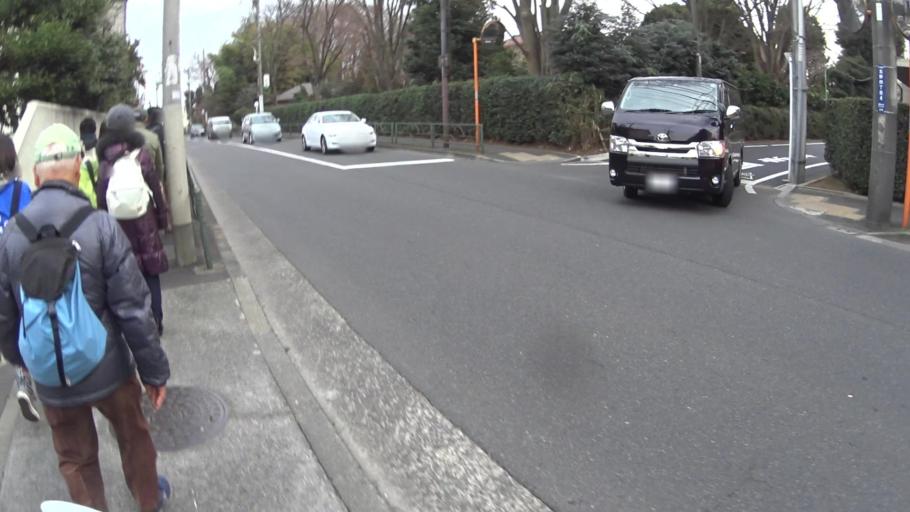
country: JP
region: Tokyo
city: Mitaka-shi
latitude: 35.6716
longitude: 139.5883
